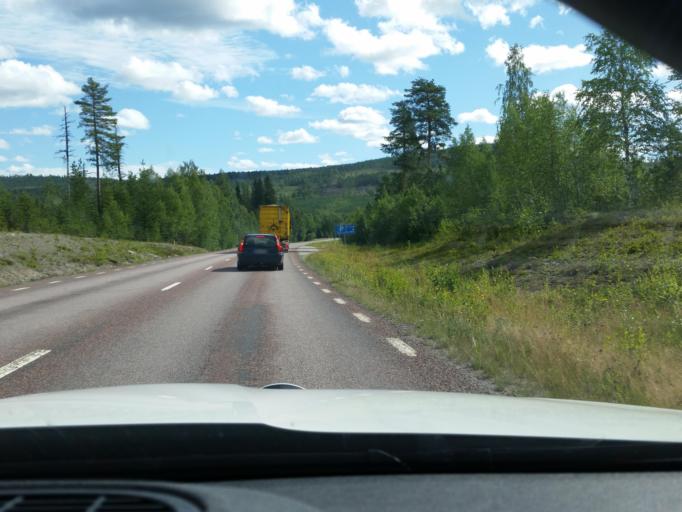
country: SE
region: Norrbotten
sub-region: Alvsbyns Kommun
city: AElvsbyn
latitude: 65.6755
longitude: 21.1978
